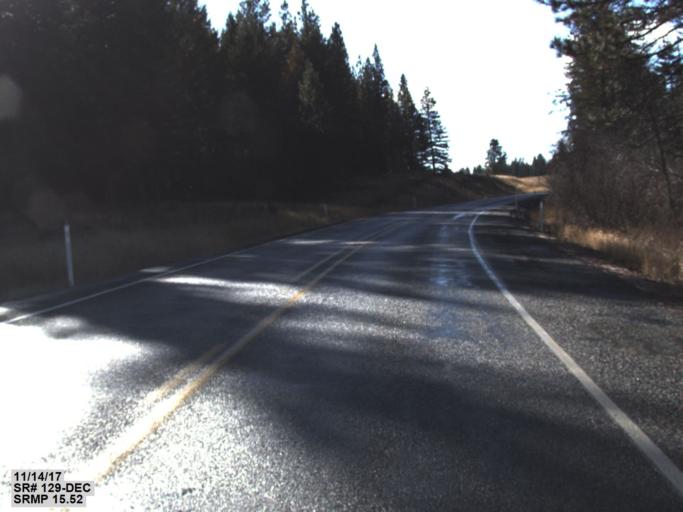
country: US
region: Washington
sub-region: Asotin County
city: Asotin
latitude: 46.1071
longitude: -117.1391
